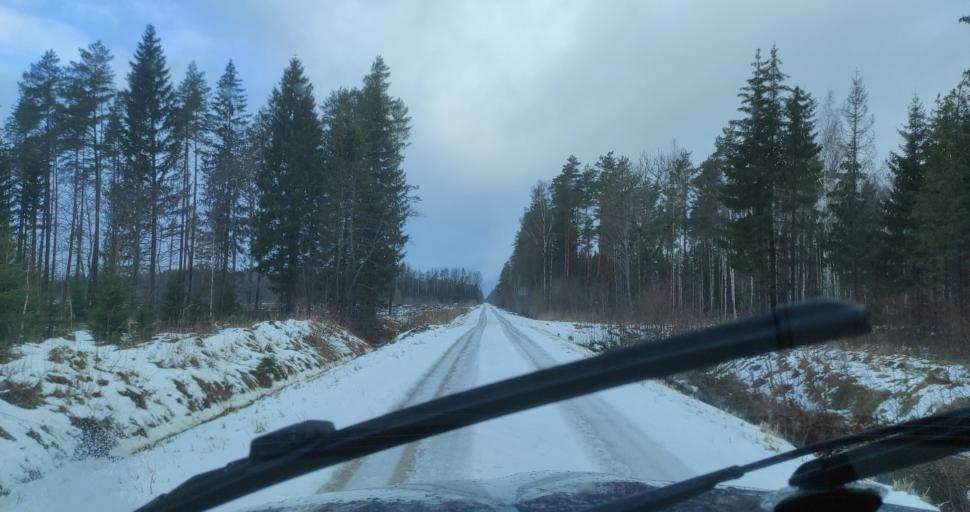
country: LV
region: Dundaga
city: Dundaga
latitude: 57.4018
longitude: 22.1042
